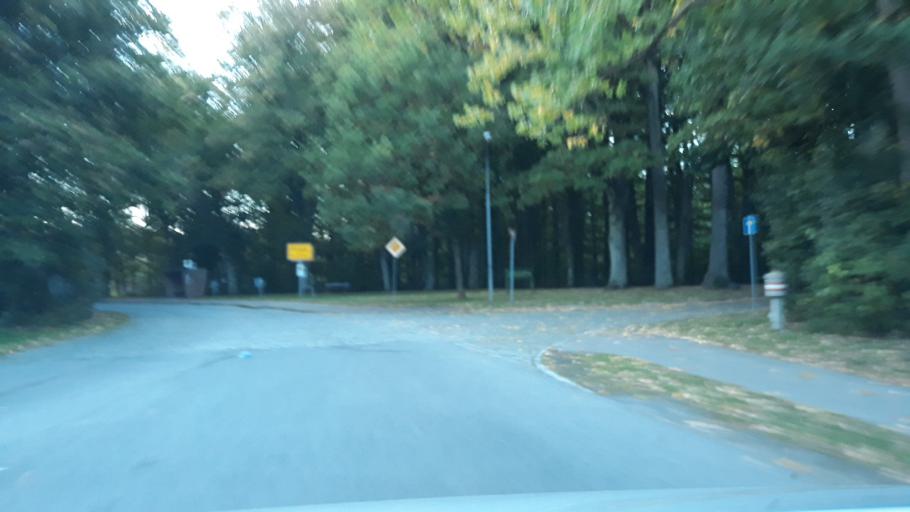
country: DE
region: Schleswig-Holstein
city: Kropp
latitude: 54.4056
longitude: 9.5254
